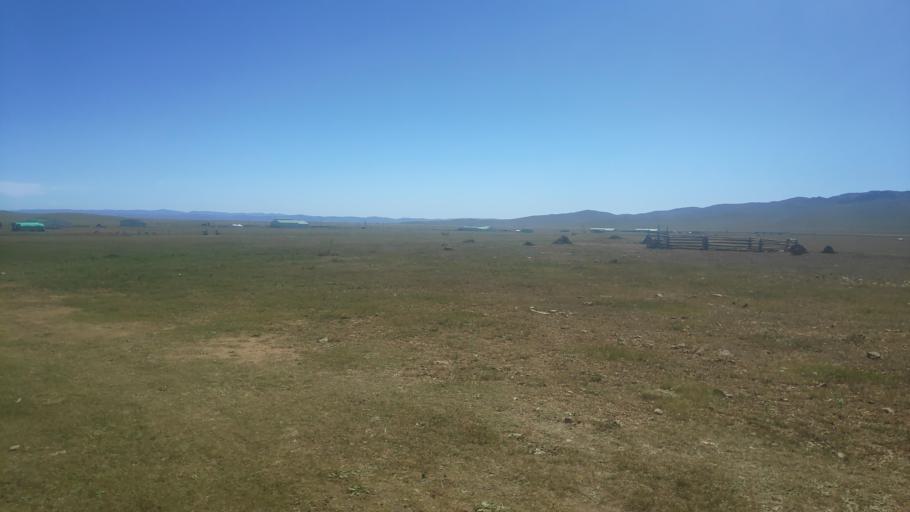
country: MN
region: Central Aimak
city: Bayandelger
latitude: 47.7289
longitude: 108.0285
